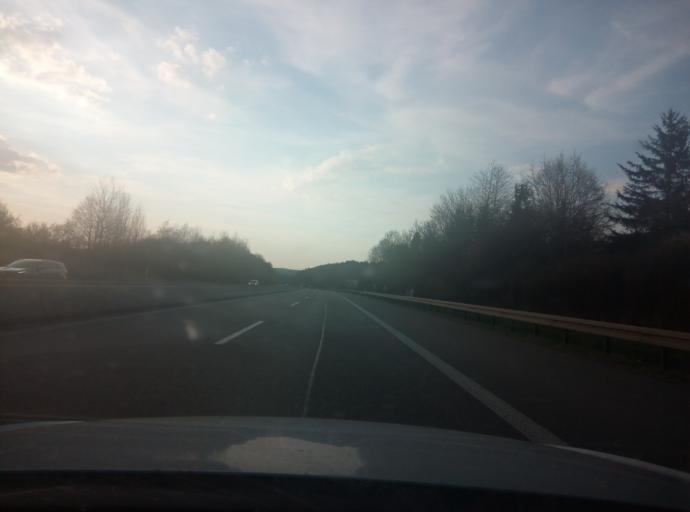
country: DE
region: Baden-Wuerttemberg
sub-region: Freiburg Region
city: Trossingen
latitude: 48.0610
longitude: 8.6179
